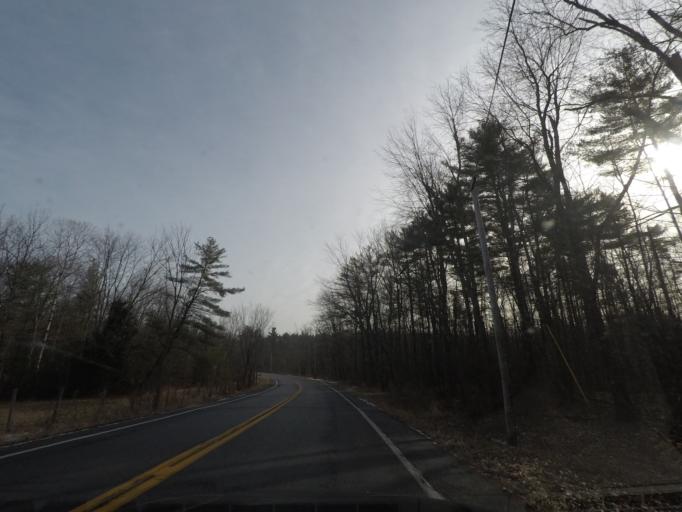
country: US
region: New York
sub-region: Saratoga County
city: Stillwater
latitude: 42.9917
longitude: -73.7126
